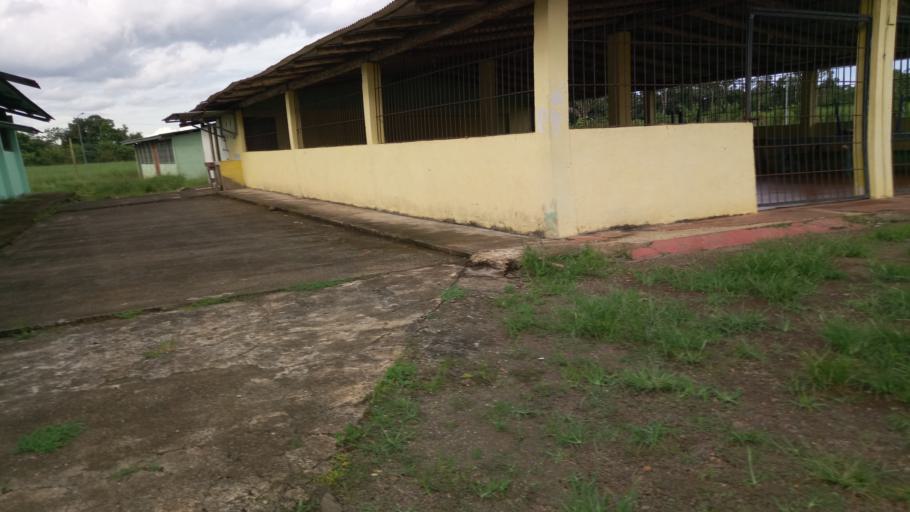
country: CR
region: Alajuela
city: Quesada
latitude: 10.4188
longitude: -84.4688
